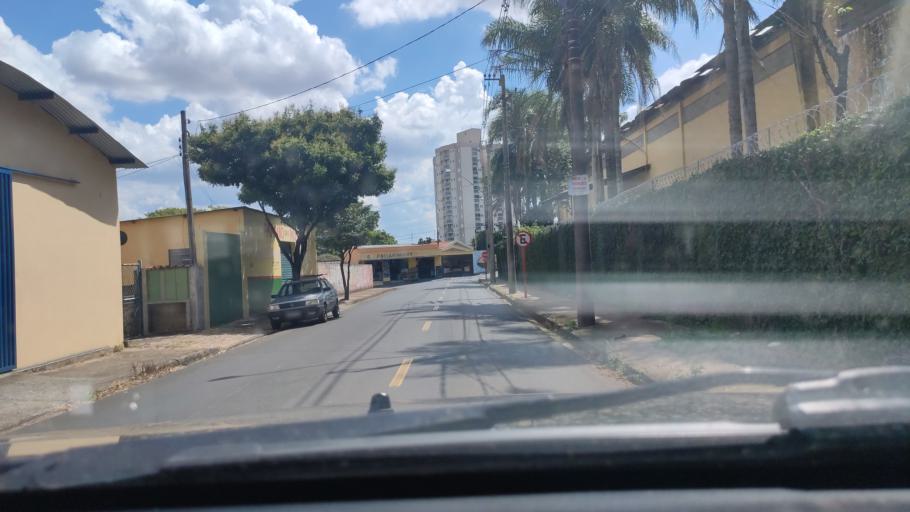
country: BR
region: Sao Paulo
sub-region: Sao Carlos
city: Sao Carlos
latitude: -22.0055
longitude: -47.8795
